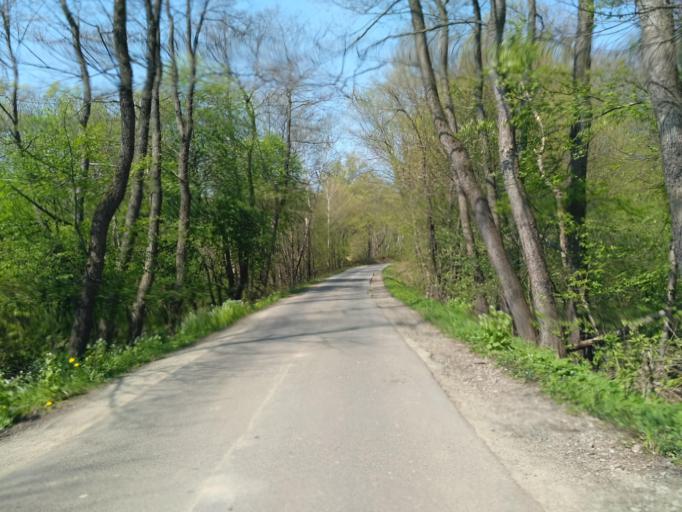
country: PL
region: Subcarpathian Voivodeship
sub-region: Powiat krosnienski
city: Chorkowka
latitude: 49.6141
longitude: 21.7172
